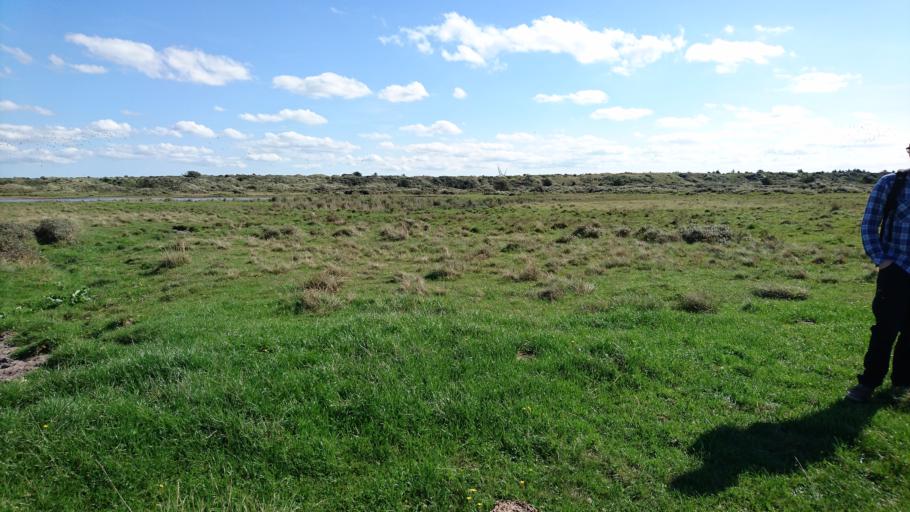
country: DK
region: North Denmark
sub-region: Hjorring Kommune
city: Hirtshals
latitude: 57.5188
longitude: 9.8763
